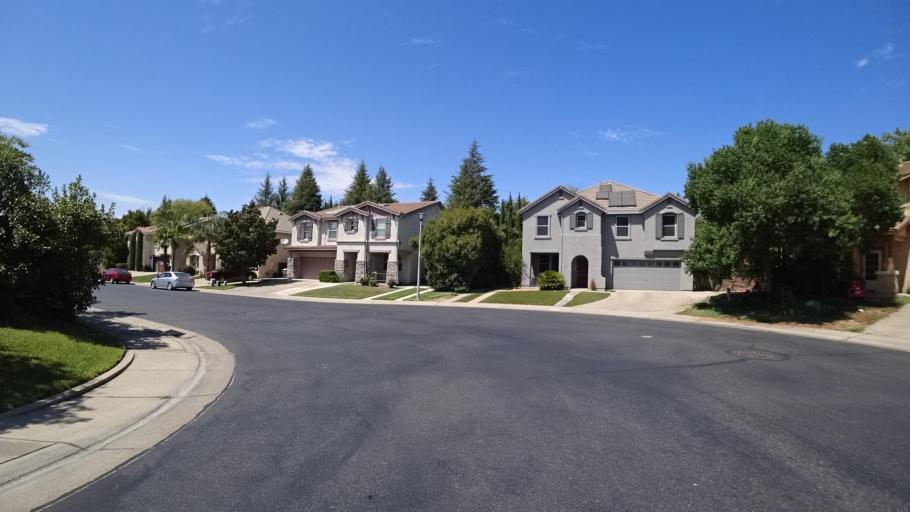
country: US
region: California
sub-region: Placer County
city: Rocklin
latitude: 38.8062
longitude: -121.2781
